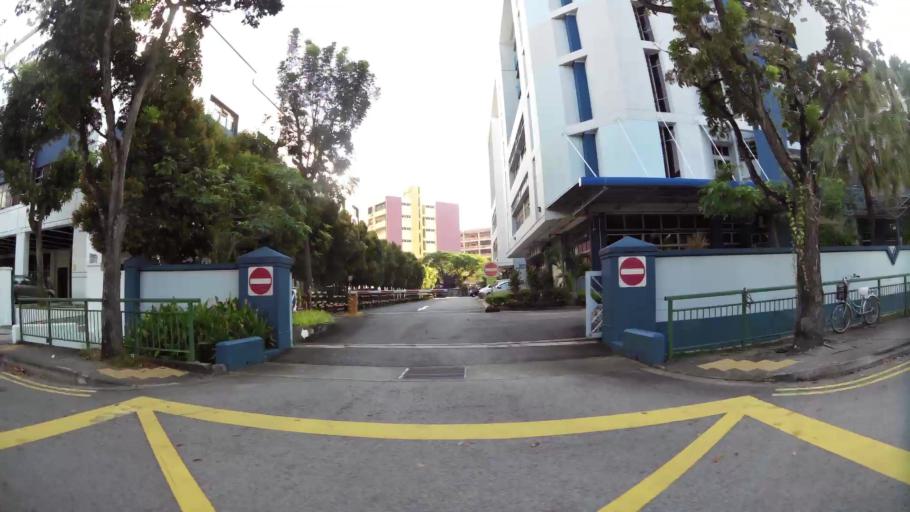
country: SG
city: Singapore
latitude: 1.3240
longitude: 103.8782
